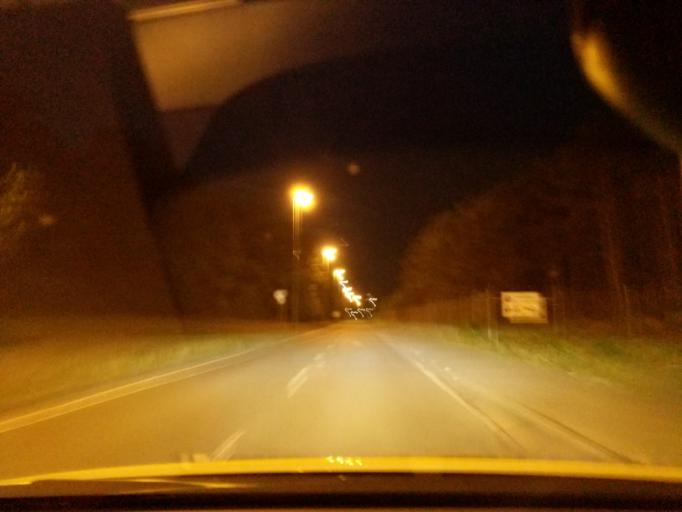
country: DE
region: Rheinland-Pfalz
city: Rodenbach
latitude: 49.4412
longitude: 7.6940
